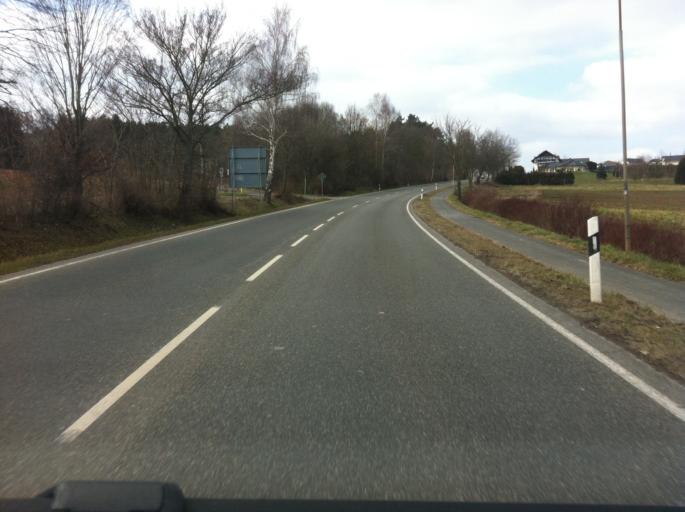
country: DE
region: North Rhine-Westphalia
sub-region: Regierungsbezirk Koln
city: Mechernich
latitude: 50.5854
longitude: 6.6687
